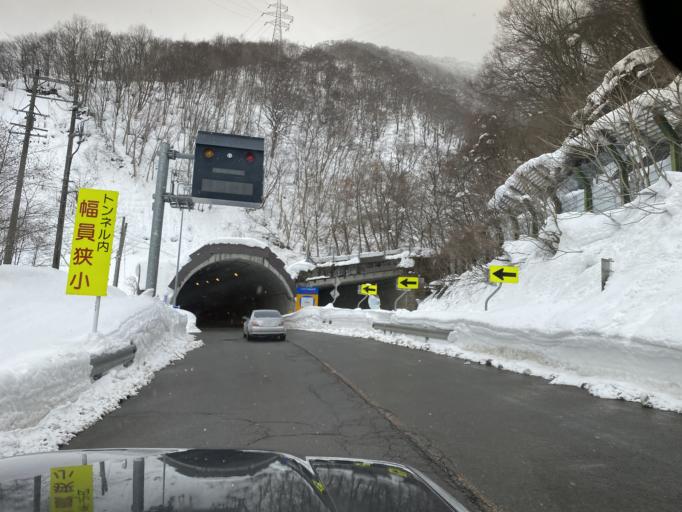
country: JP
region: Gifu
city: Takayama
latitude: 36.1408
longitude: 136.9066
